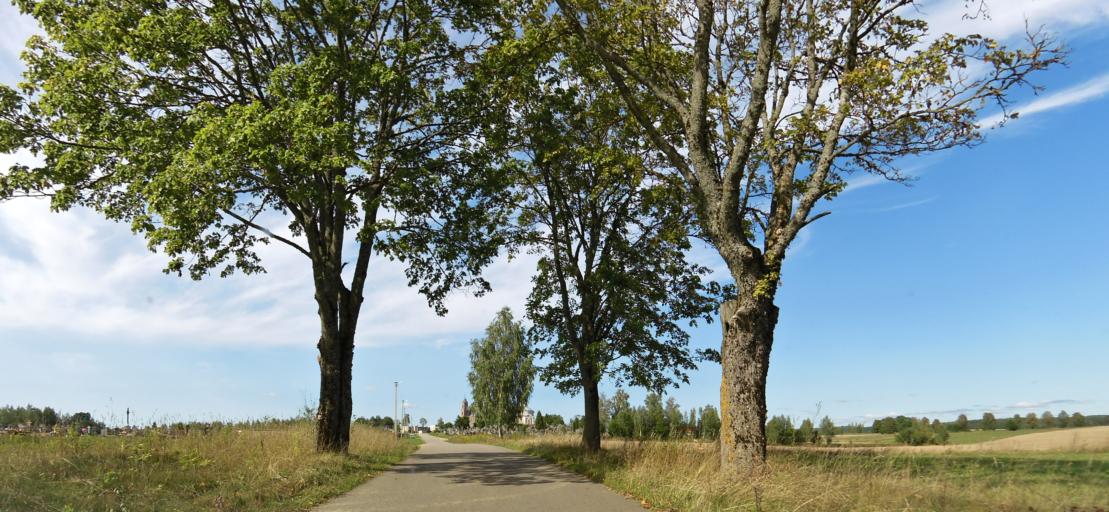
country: LT
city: Salcininkai
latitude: 54.4511
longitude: 25.5137
